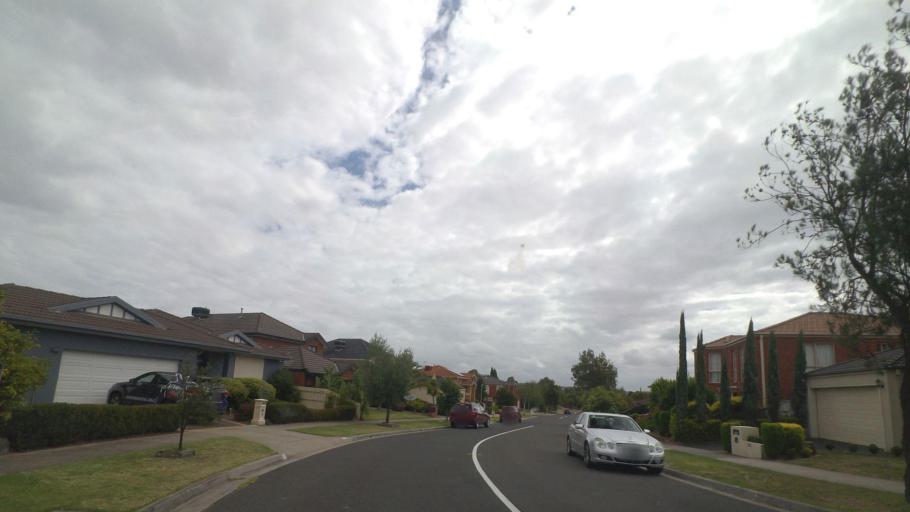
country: AU
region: Victoria
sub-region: Knox
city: Wantirna South
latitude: -37.8867
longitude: 145.2191
